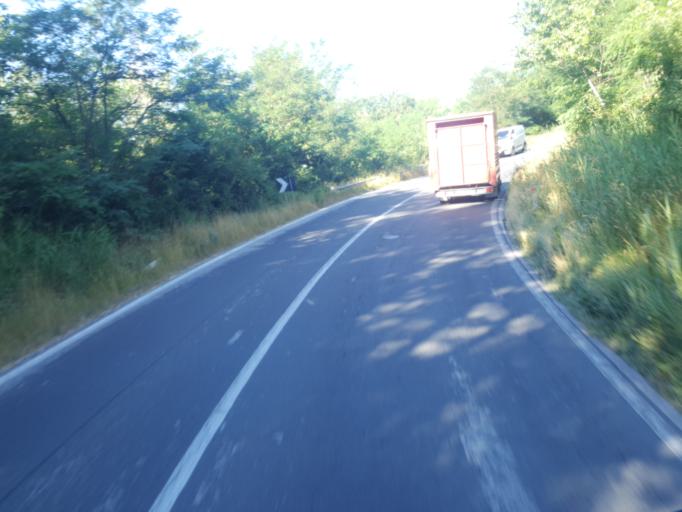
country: IT
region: The Marches
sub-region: Provincia di Pesaro e Urbino
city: Montecalvo in Foglia
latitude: 43.8008
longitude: 12.6581
